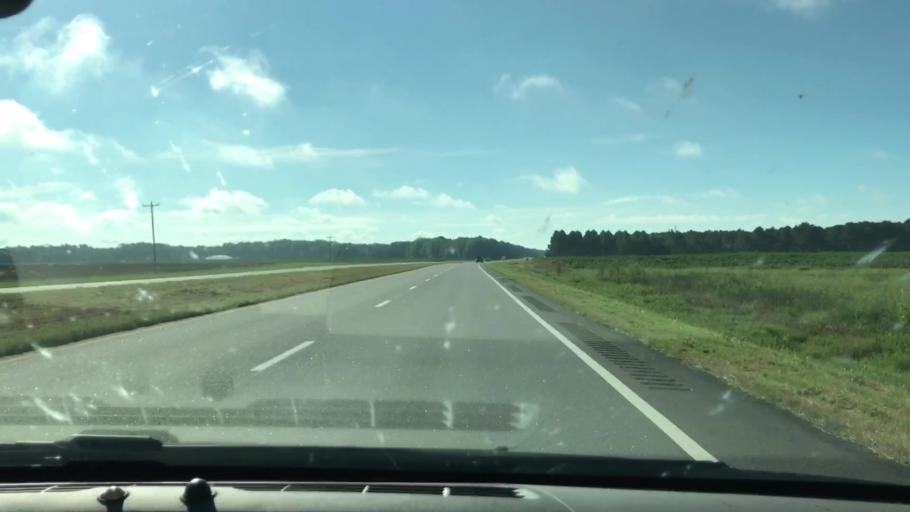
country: US
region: Georgia
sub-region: Terrell County
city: Dawson
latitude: 31.6990
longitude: -84.3228
